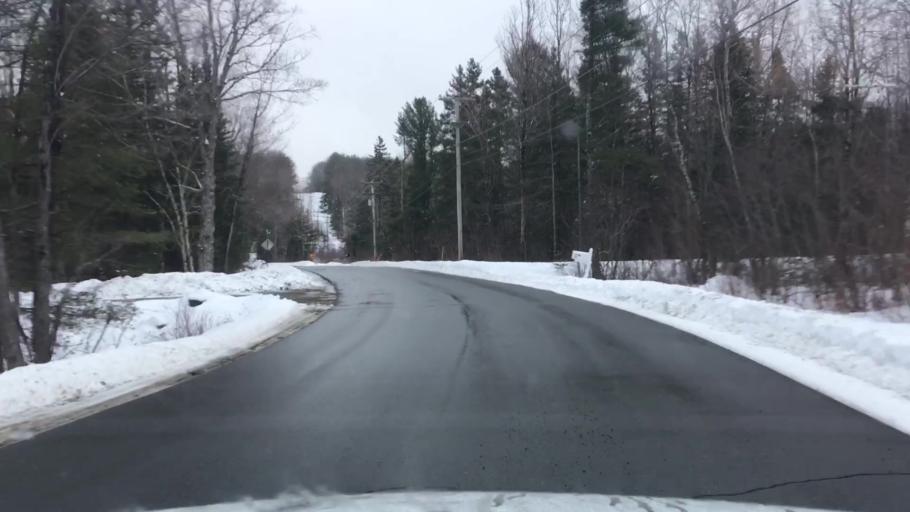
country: US
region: Maine
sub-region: Hancock County
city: Trenton
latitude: 44.4066
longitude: -68.3217
